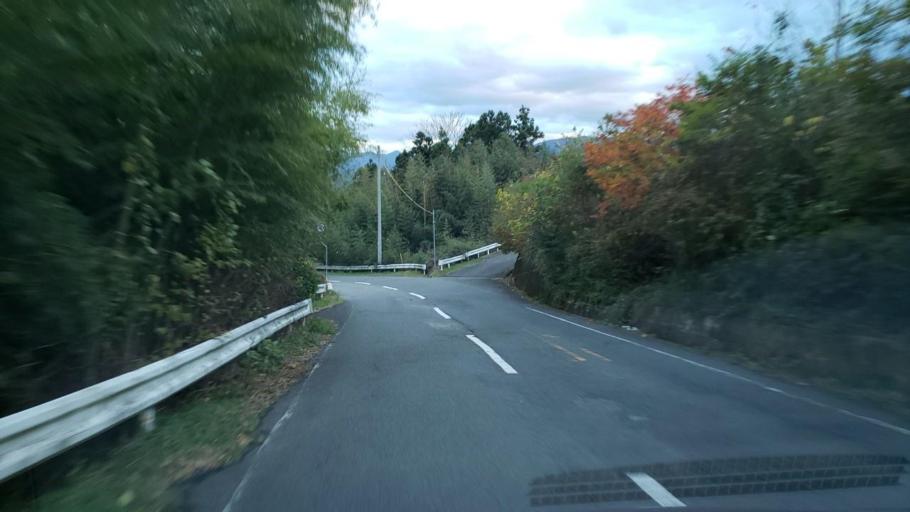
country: JP
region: Tokushima
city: Wakimachi
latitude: 34.0858
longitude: 134.1832
